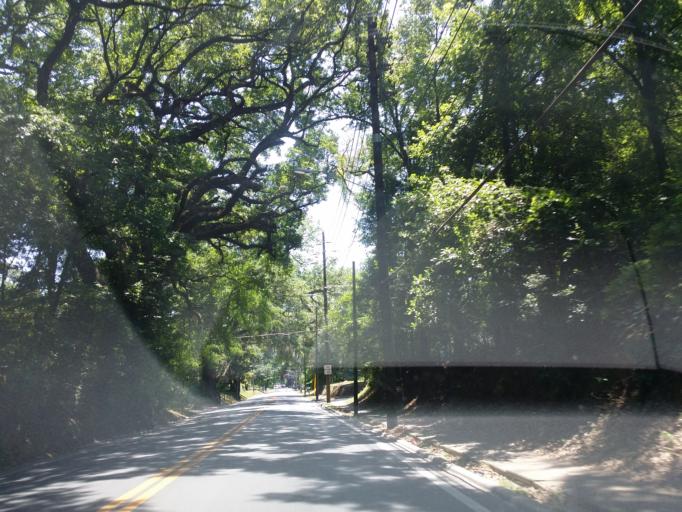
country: US
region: Florida
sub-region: Leon County
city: Tallahassee
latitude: 30.4559
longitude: -84.2943
